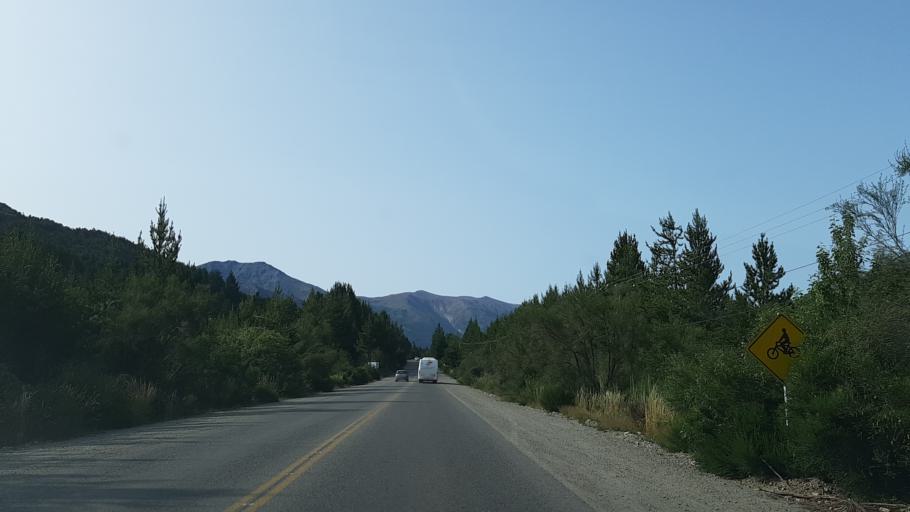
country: AR
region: Rio Negro
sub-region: Departamento de Bariloche
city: San Carlos de Bariloche
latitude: -41.1450
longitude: -71.4102
